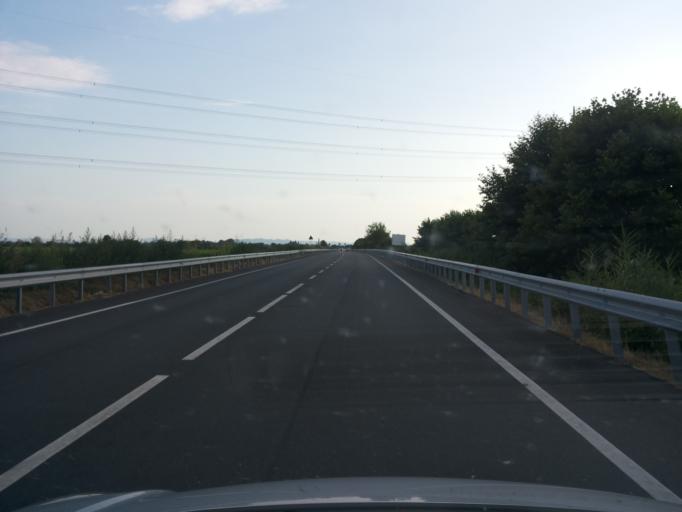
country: IT
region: Piedmont
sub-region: Provincia di Vercelli
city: Desana
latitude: 45.2861
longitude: 8.3763
